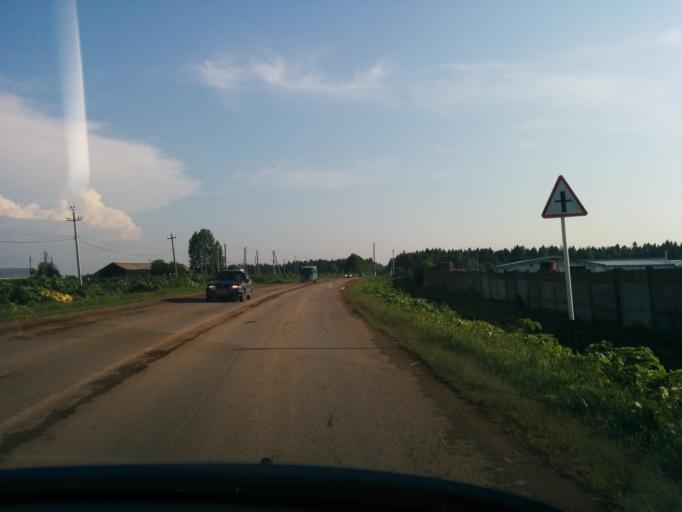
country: RU
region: Perm
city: Polazna
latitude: 58.2221
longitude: 56.2976
